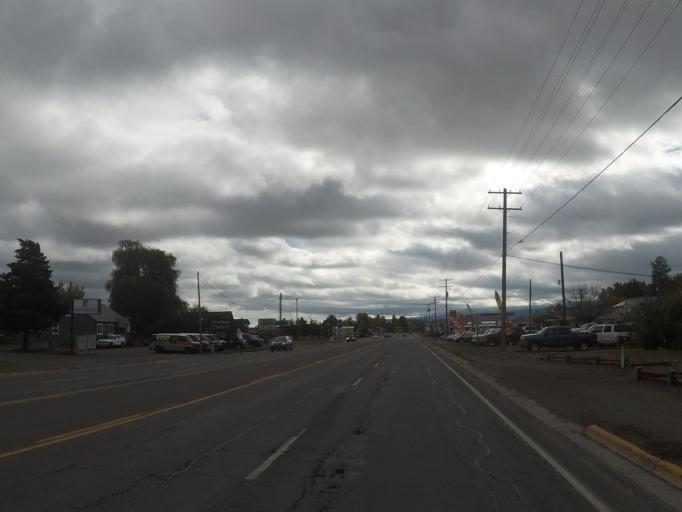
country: US
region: Montana
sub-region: Flathead County
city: Evergreen
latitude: 48.2203
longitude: -114.2774
